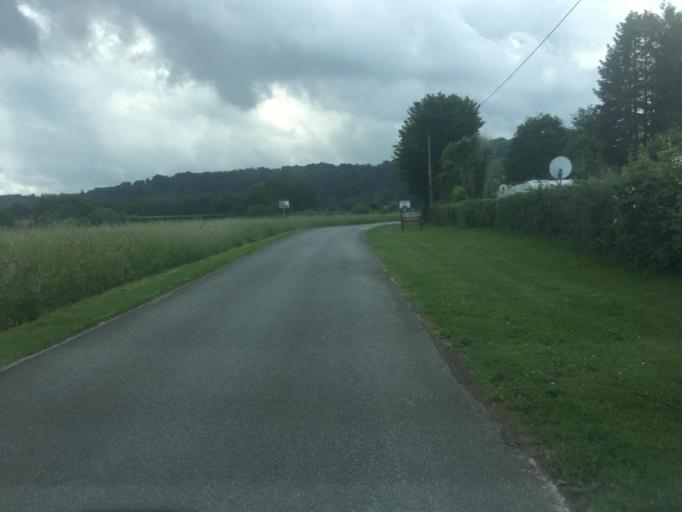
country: BE
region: Wallonia
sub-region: Province du Luxembourg
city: Florenville
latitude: 49.7118
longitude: 5.2612
